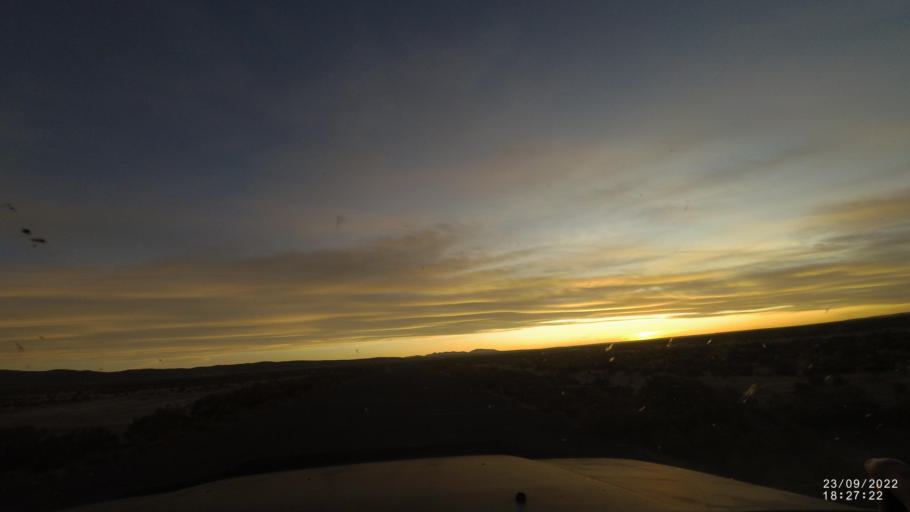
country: BO
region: Oruro
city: Challapata
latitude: -19.3276
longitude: -67.1664
